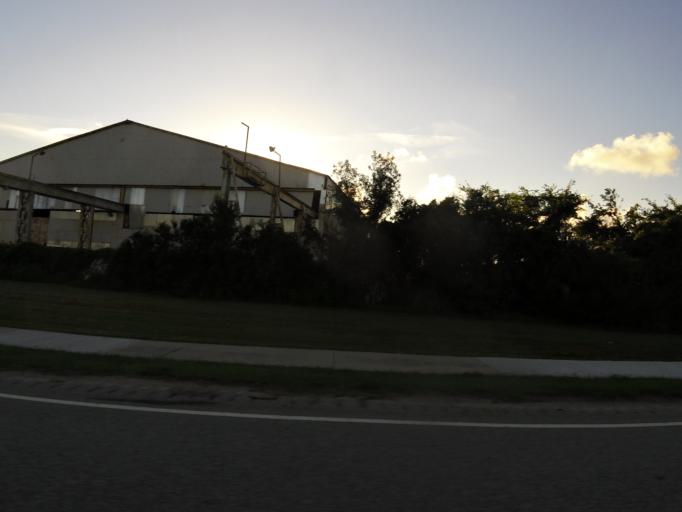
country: US
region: Georgia
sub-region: Glynn County
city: Brunswick
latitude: 31.1292
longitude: -81.4799
